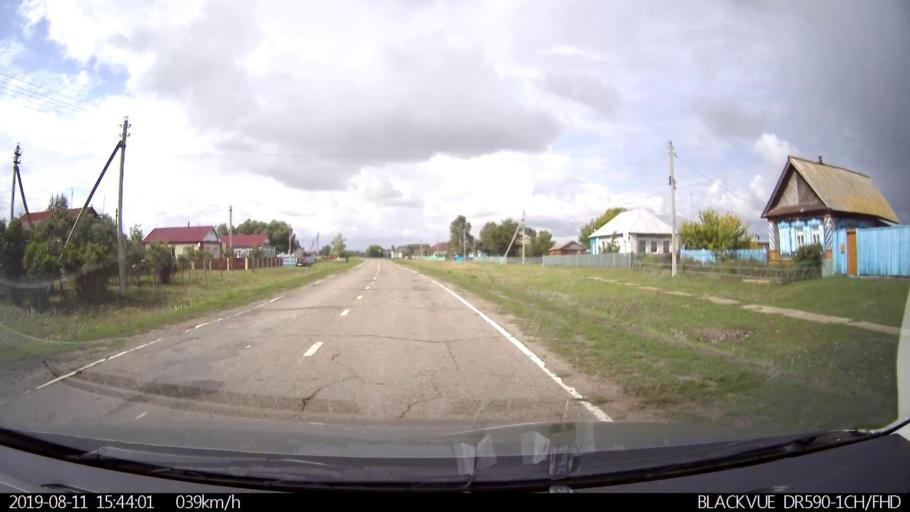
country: RU
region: Ulyanovsk
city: Ignatovka
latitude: 53.8795
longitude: 47.6581
